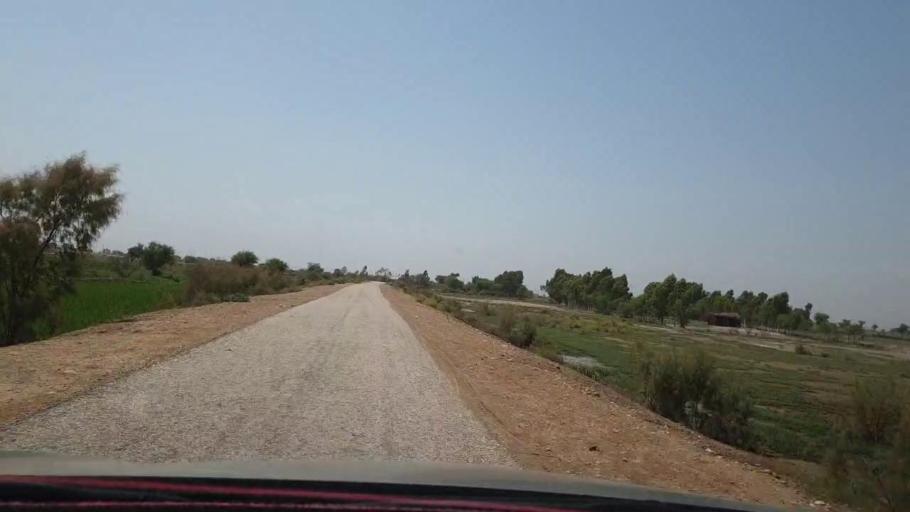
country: PK
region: Sindh
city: Warah
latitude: 27.5077
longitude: 67.7176
